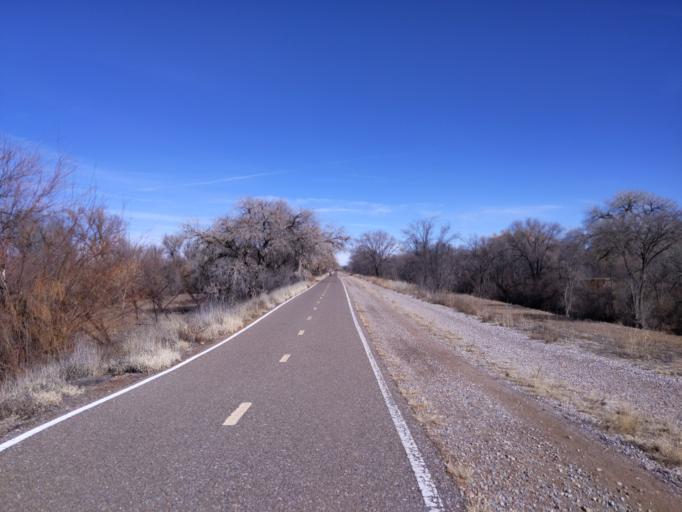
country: US
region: New Mexico
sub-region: Bernalillo County
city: Lee Acres
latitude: 35.1525
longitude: -106.6701
